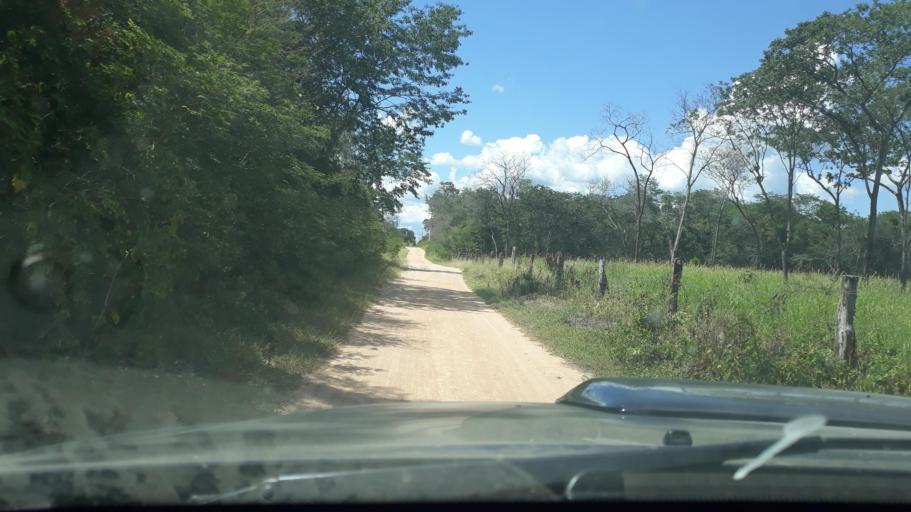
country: BR
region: Bahia
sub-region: Riacho De Santana
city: Riacho de Santana
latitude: -13.8661
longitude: -43.0179
